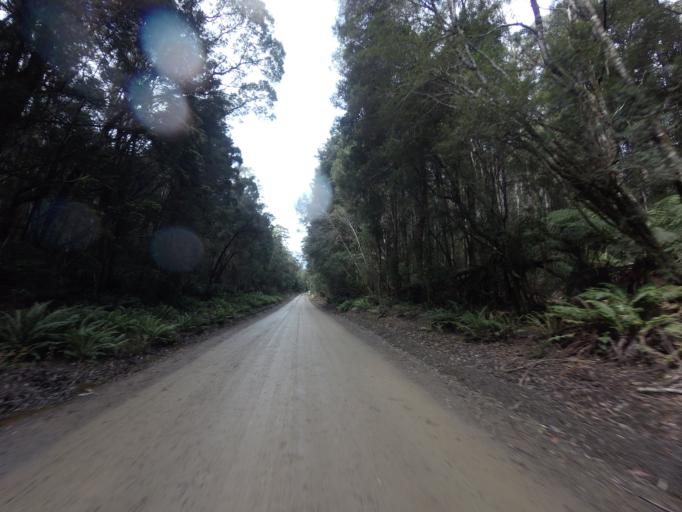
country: AU
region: Tasmania
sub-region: Huon Valley
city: Geeveston
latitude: -43.3947
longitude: 146.8574
